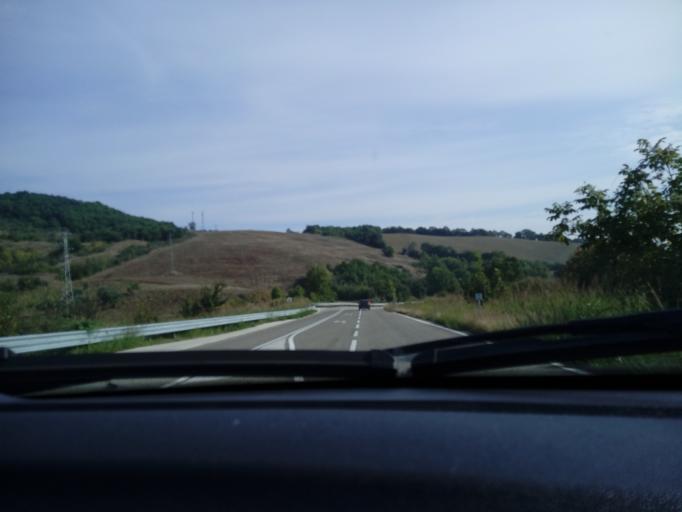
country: IT
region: Molise
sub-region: Provincia di Campobasso
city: Riccia
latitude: 41.5246
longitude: 14.8566
